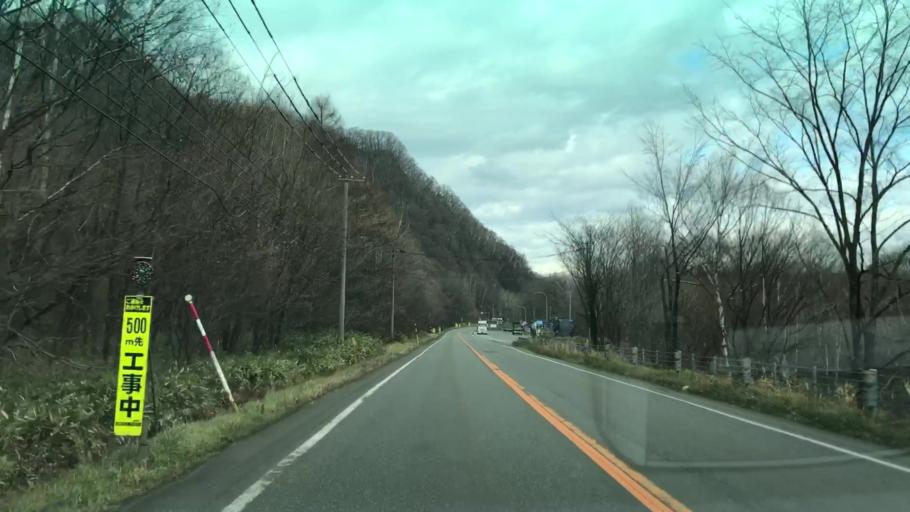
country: JP
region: Hokkaido
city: Shizunai-furukawacho
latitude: 42.8361
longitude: 142.4156
